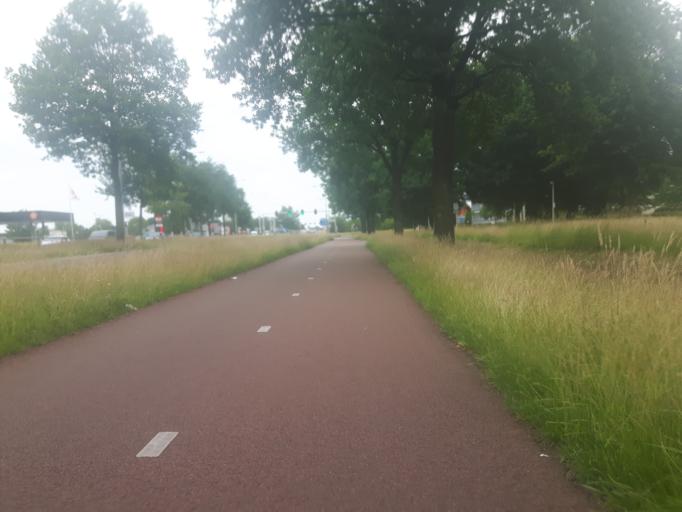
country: NL
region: Overijssel
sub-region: Gemeente Hengelo
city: Hengelo
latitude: 52.2829
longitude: 6.7767
